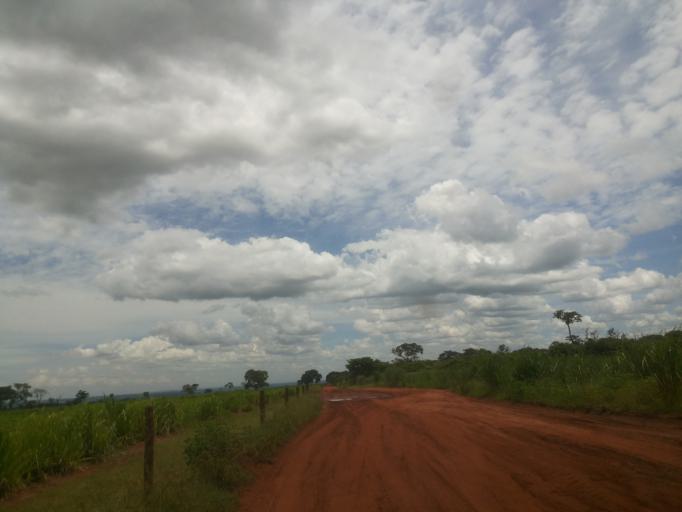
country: BR
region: Minas Gerais
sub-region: Santa Vitoria
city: Santa Vitoria
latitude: -18.7291
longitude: -49.9686
